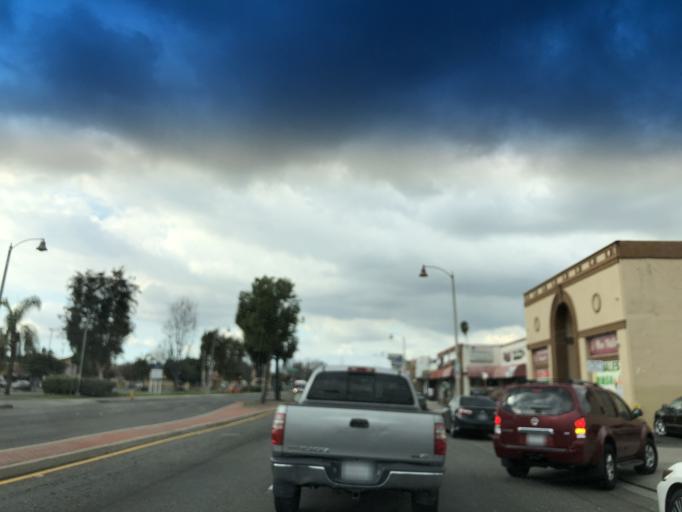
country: US
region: California
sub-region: Los Angeles County
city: Pico Rivera
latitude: 33.9996
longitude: -118.0796
